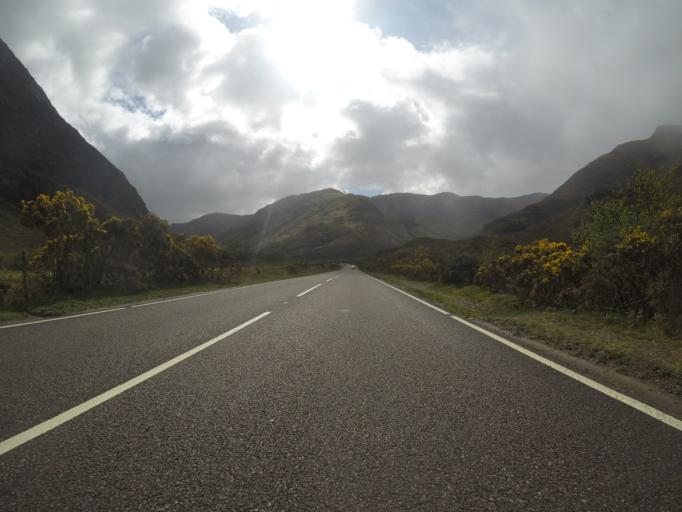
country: GB
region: Scotland
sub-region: Highland
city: Fort William
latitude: 57.1744
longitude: -5.3623
